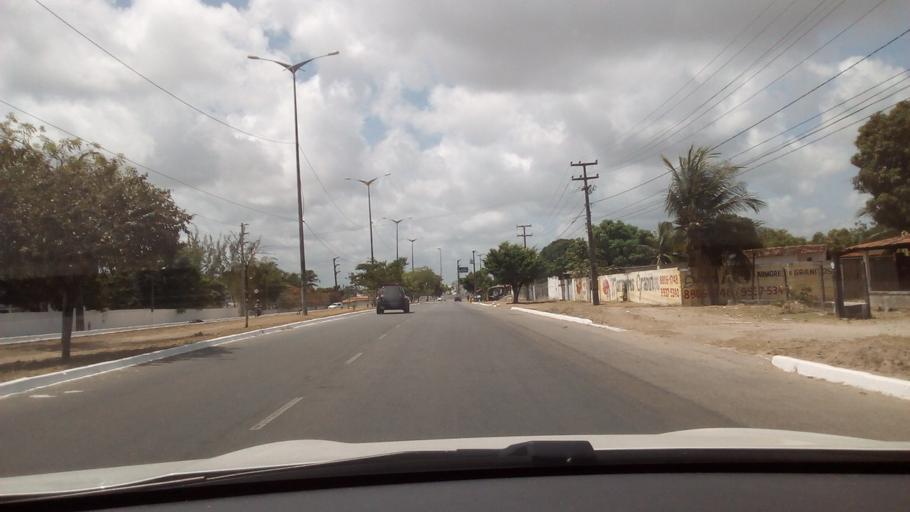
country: BR
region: Paraiba
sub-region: Joao Pessoa
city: Joao Pessoa
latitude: -7.1620
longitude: -34.8234
